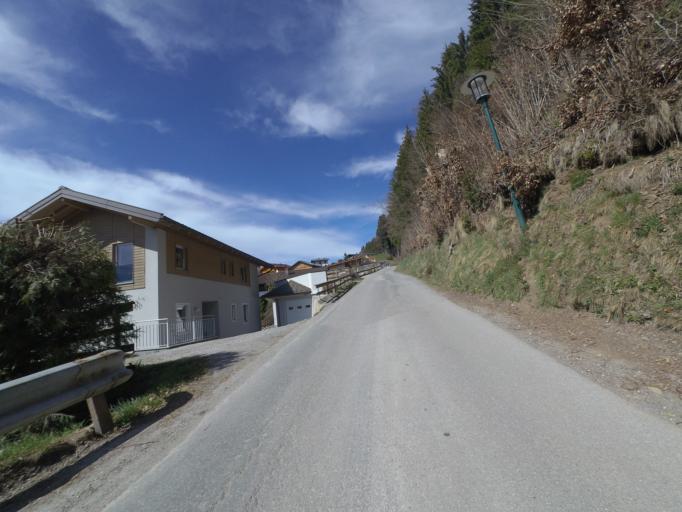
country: AT
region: Salzburg
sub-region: Politischer Bezirk Sankt Johann im Pongau
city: Sankt Veit im Pongau
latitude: 47.3343
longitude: 13.1446
